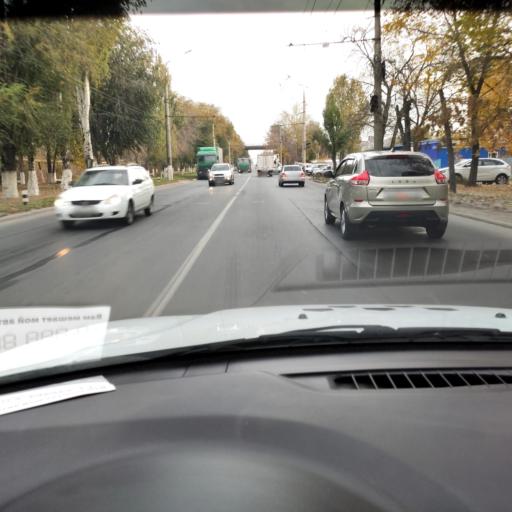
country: RU
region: Samara
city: Tol'yatti
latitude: 53.5567
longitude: 49.4518
